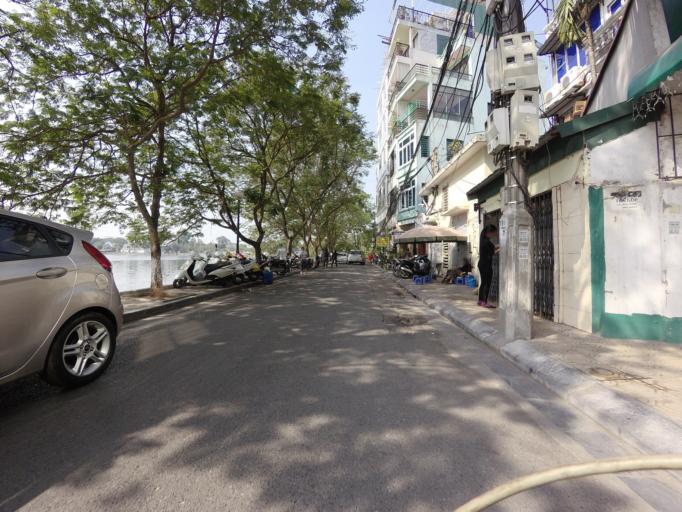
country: VN
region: Ha Noi
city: Hoan Kiem
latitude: 21.0483
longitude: 105.8408
